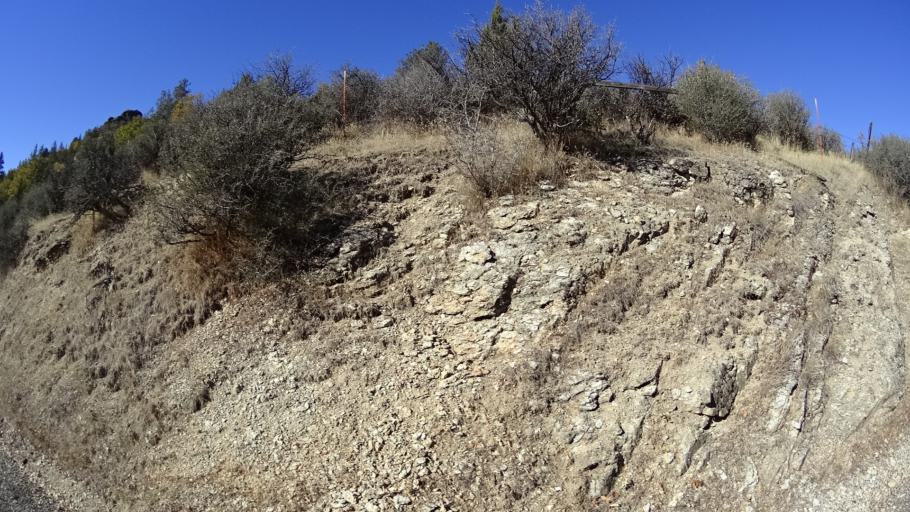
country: US
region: California
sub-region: Siskiyou County
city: Montague
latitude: 41.9360
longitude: -122.3542
